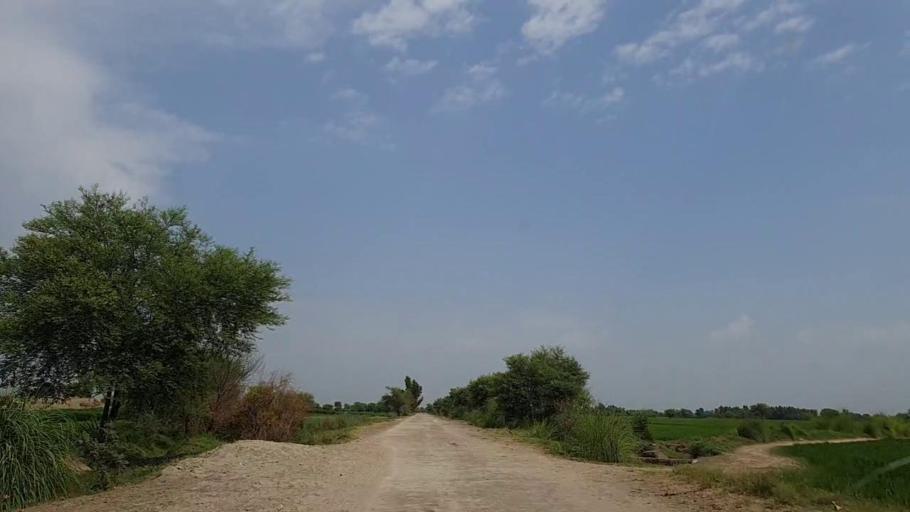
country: PK
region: Sindh
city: Khanpur
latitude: 27.8456
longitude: 69.4588
